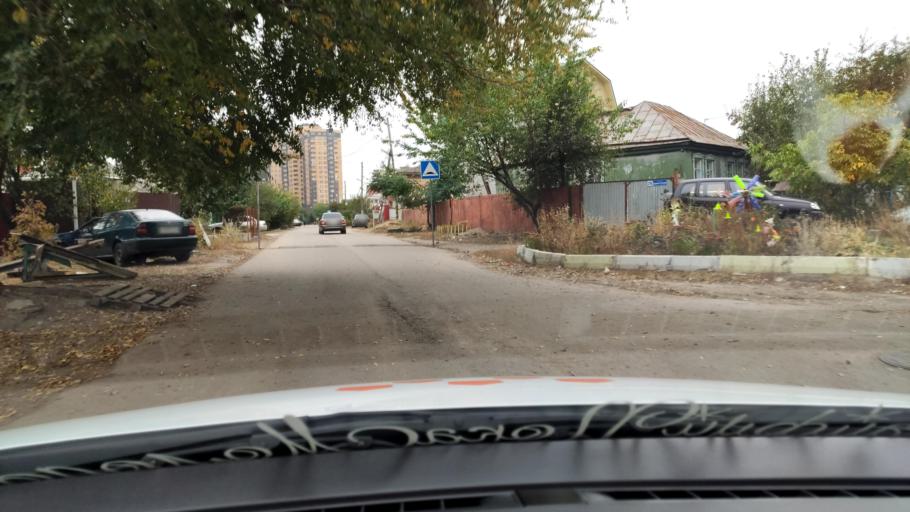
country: RU
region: Voronezj
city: Voronezh
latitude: 51.6767
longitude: 39.1611
